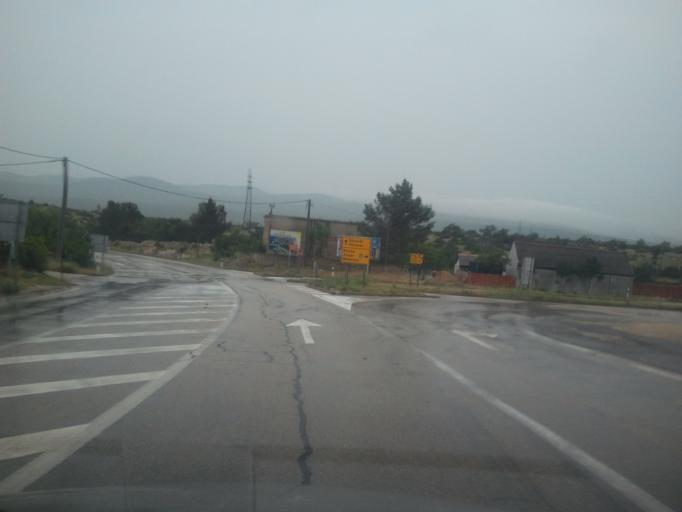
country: HR
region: Zadarska
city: Obrovac
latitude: 44.2152
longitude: 15.6902
